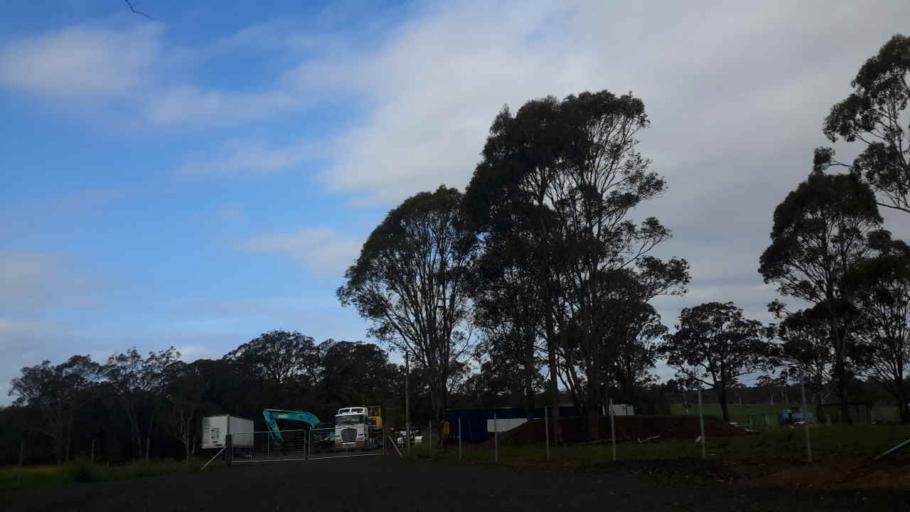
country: AU
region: New South Wales
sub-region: Wollondilly
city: Douglas Park
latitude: -34.1901
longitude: 150.7907
